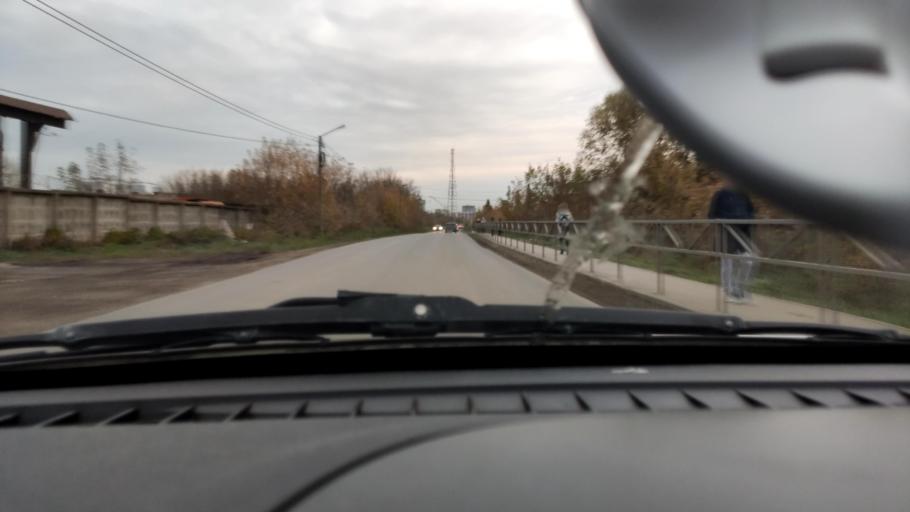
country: RU
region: Perm
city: Kondratovo
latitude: 57.9805
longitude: 56.1105
